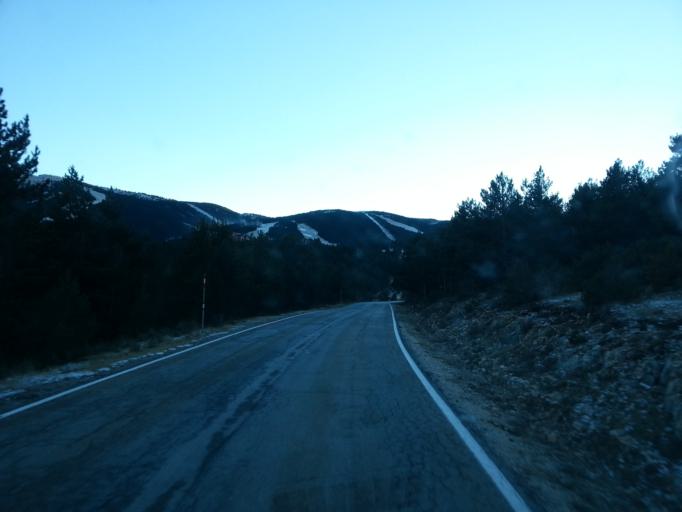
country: ES
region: Catalonia
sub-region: Provincia de Lleida
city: Gosol
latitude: 42.1818
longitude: 1.5586
